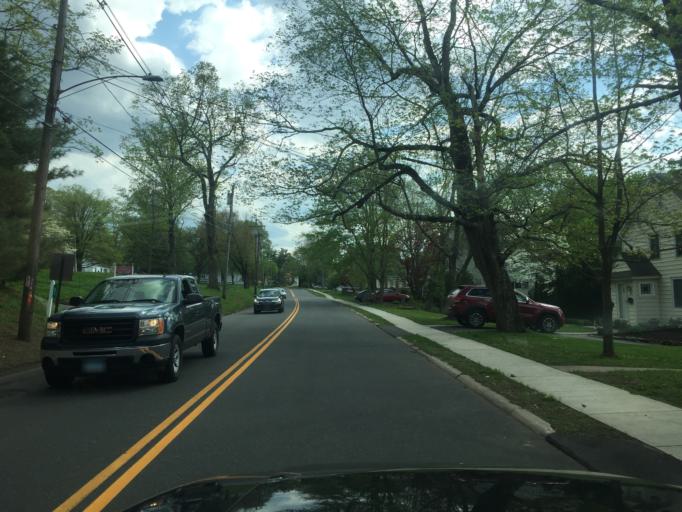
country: US
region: Connecticut
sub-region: Hartford County
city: Kensington
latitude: 41.6243
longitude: -72.7444
